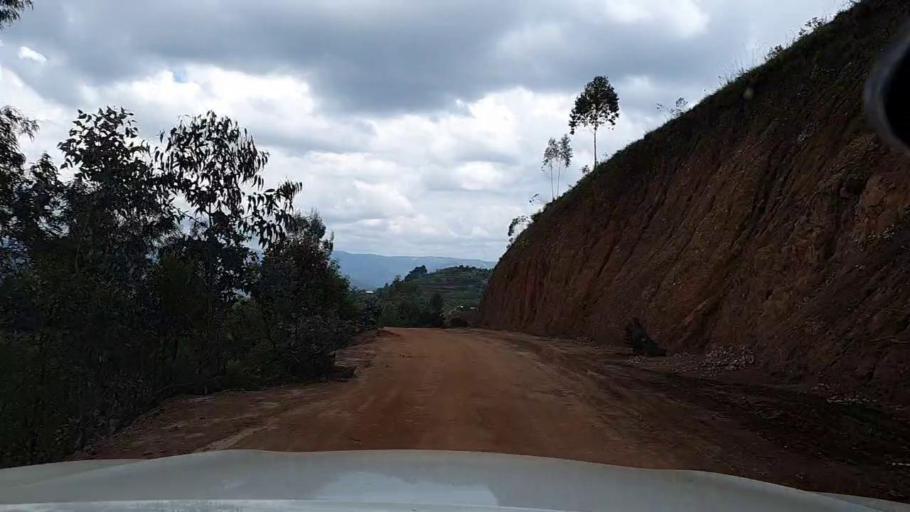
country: RW
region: Southern Province
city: Nzega
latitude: -2.7074
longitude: 29.5110
